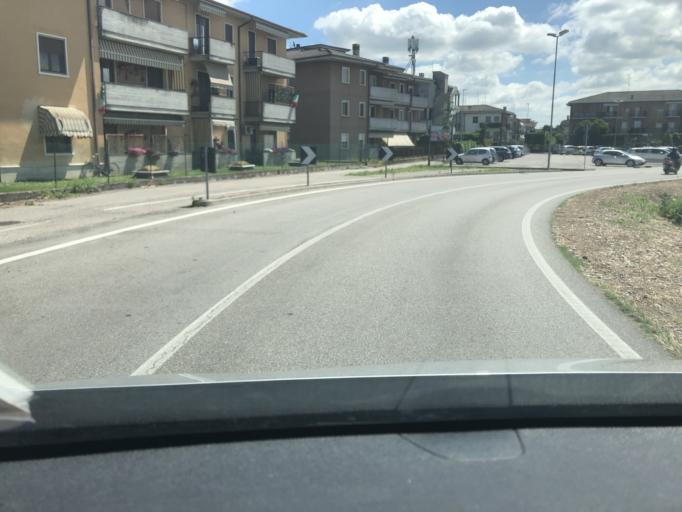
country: IT
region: Veneto
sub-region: Provincia di Verona
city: Villafranca di Verona
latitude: 45.3489
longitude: 10.8345
